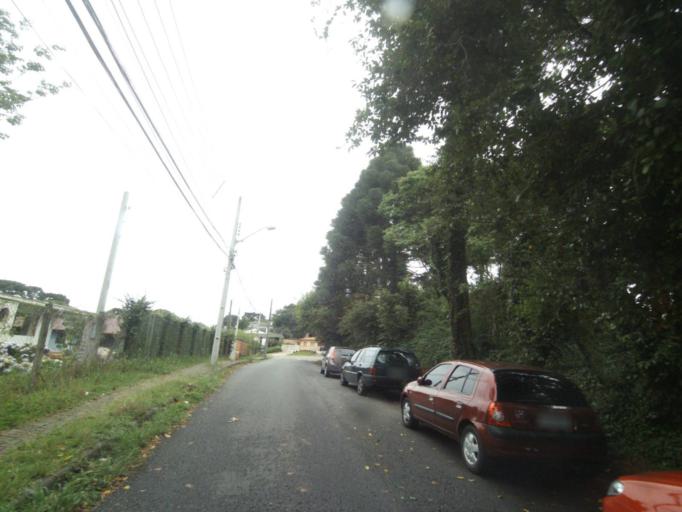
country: BR
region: Parana
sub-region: Curitiba
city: Curitiba
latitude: -25.4442
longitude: -49.3391
